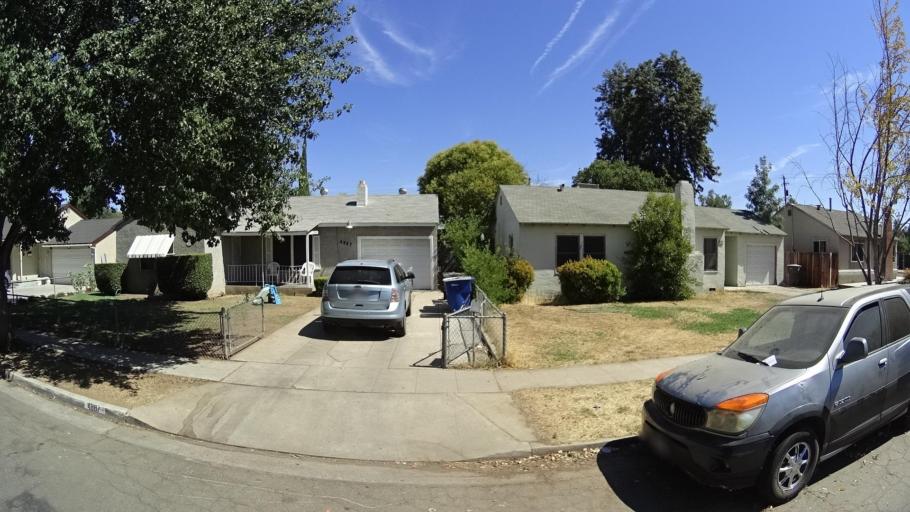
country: US
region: California
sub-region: Fresno County
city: Sunnyside
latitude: 36.7459
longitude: -119.7323
